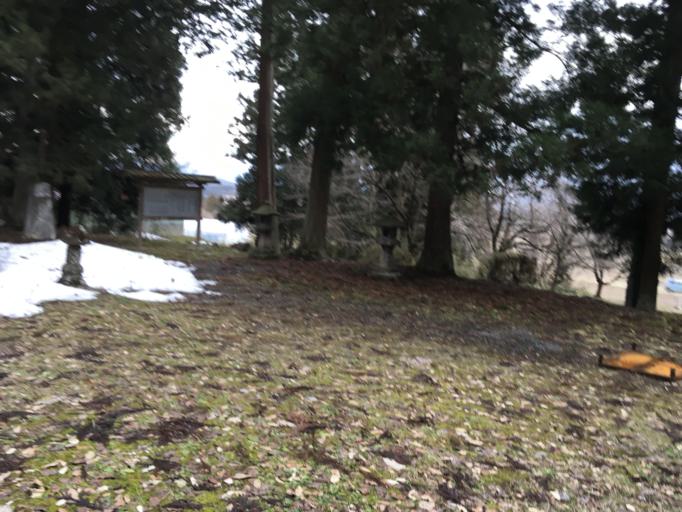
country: JP
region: Iwate
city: Kitakami
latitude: 39.2270
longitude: 141.2282
